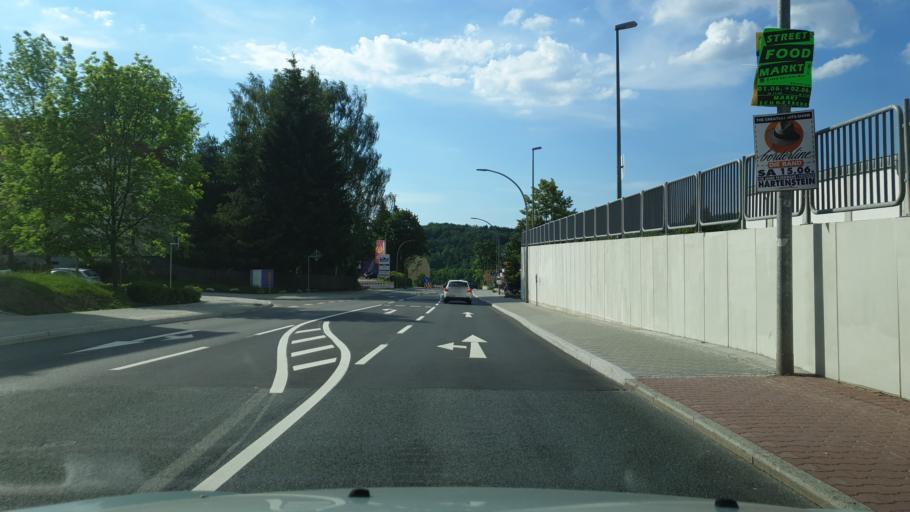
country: DE
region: Saxony
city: Aue
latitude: 50.5936
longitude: 12.7119
